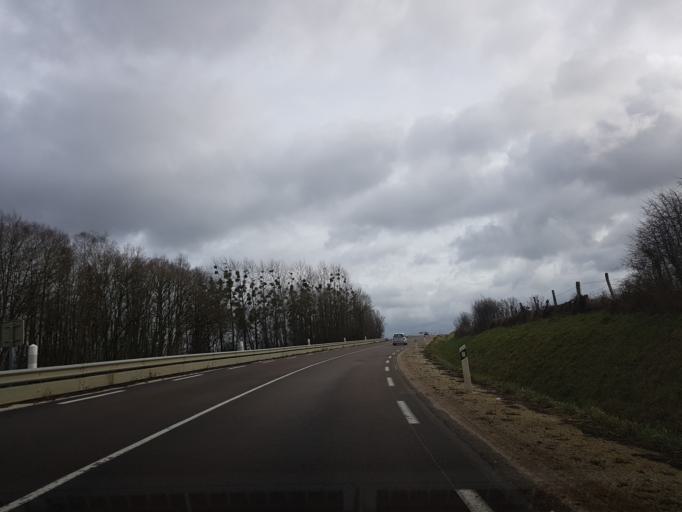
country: FR
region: Champagne-Ardenne
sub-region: Departement de la Haute-Marne
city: Langres
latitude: 47.8583
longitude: 5.3902
